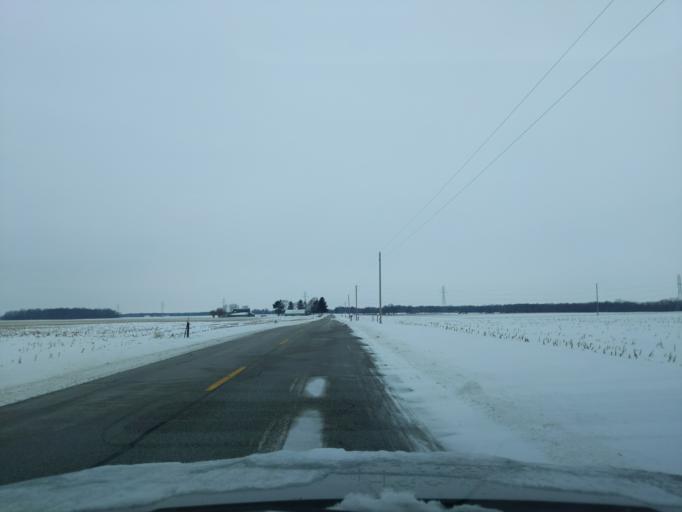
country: US
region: Indiana
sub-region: Benton County
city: Otterbein
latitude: 40.4169
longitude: -87.0769
